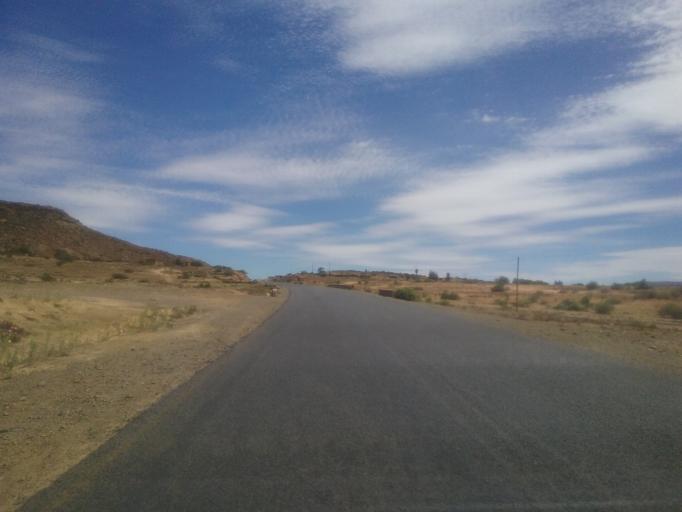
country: LS
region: Mohale's Hoek District
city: Mohale's Hoek
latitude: -30.0722
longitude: 27.4243
